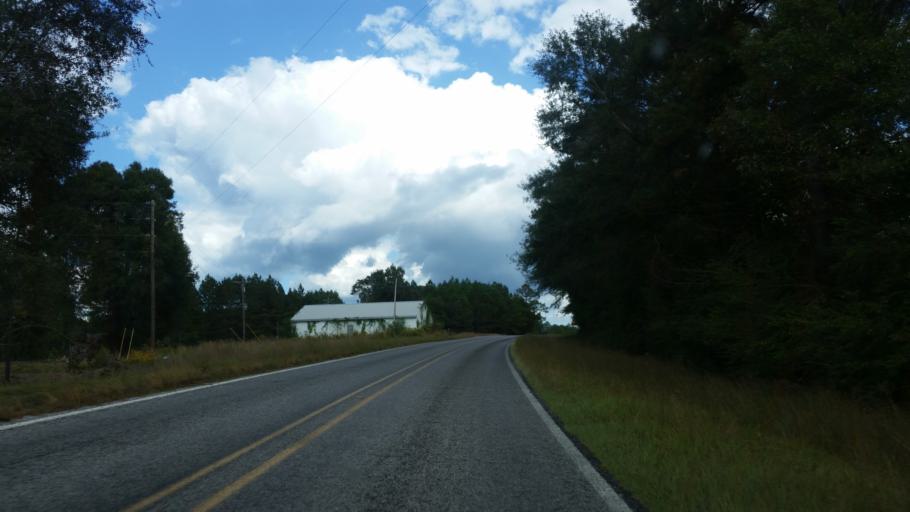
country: US
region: Mississippi
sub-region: Stone County
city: Wiggins
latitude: 30.9279
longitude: -89.0673
